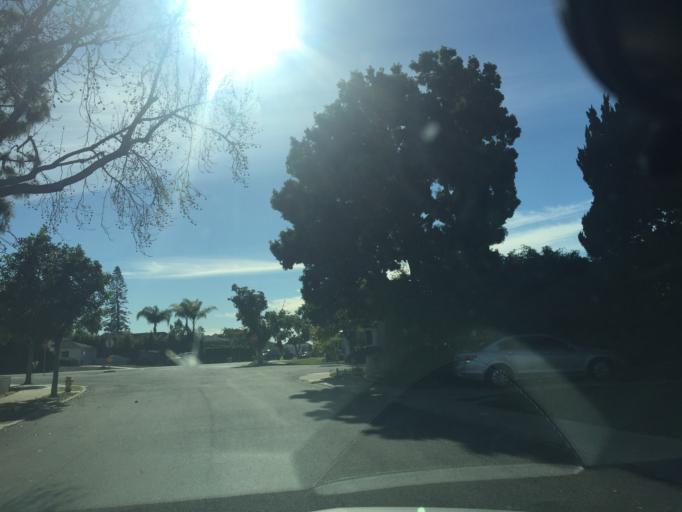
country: US
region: California
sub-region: San Diego County
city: Lemon Grove
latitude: 32.7624
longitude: -117.0917
